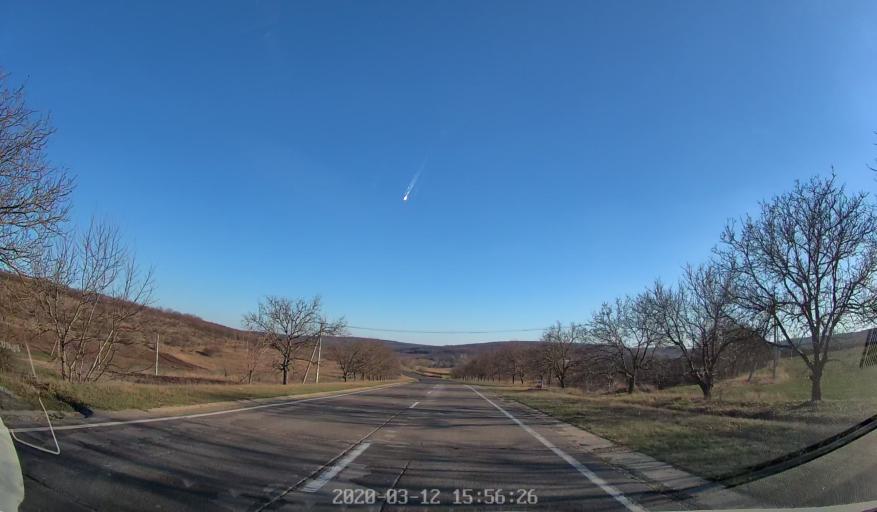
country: MD
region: Chisinau
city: Vadul lui Voda
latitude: 47.0632
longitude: 29.0330
